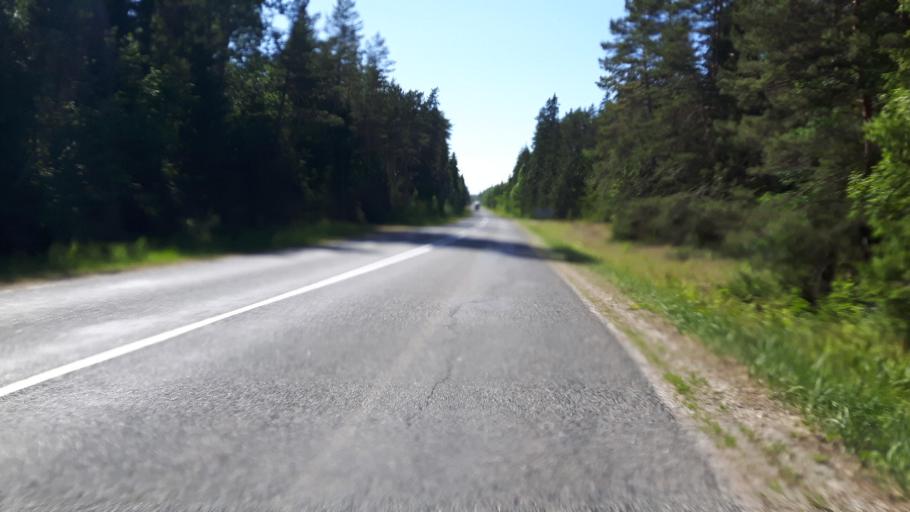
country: LV
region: Talsu Rajons
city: Stende
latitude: 57.0861
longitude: 22.4184
